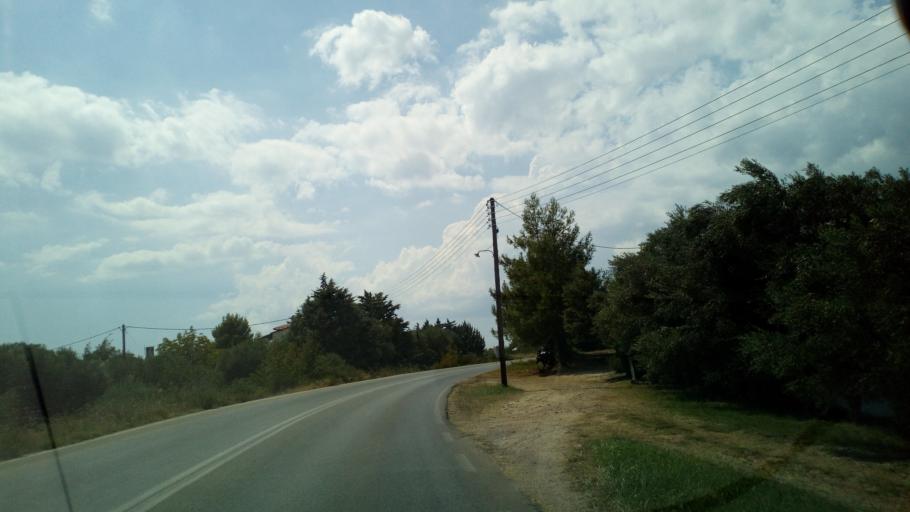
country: GR
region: Central Macedonia
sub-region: Nomos Chalkidikis
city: Nikiti
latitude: 40.2271
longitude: 23.6434
